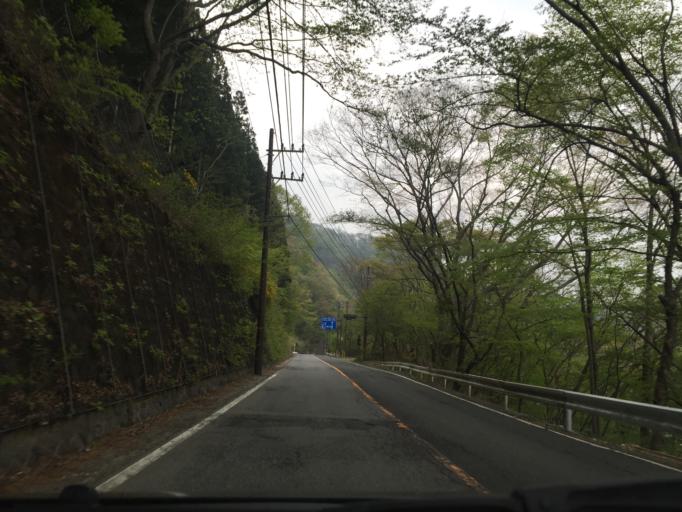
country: JP
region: Tochigi
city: Nikko
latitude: 36.9058
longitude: 139.7023
